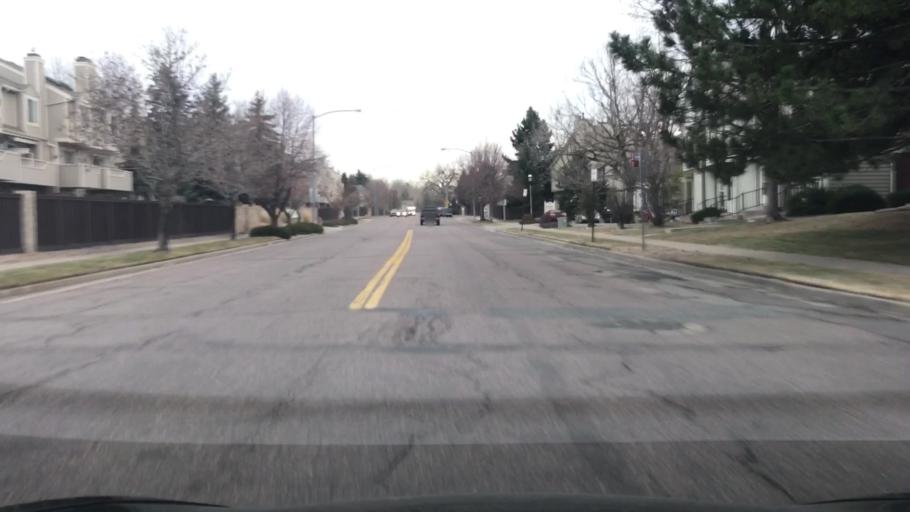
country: US
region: Colorado
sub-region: Arapahoe County
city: Glendale
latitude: 39.6846
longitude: -104.8923
